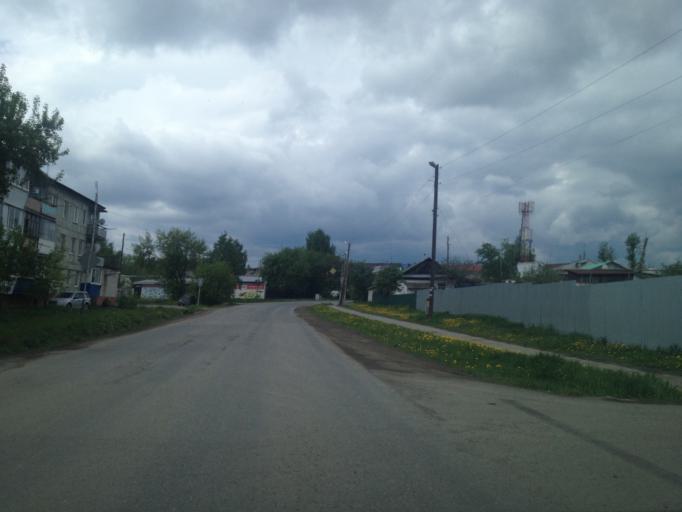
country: RU
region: Sverdlovsk
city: Aramil
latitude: 56.6858
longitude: 60.8462
